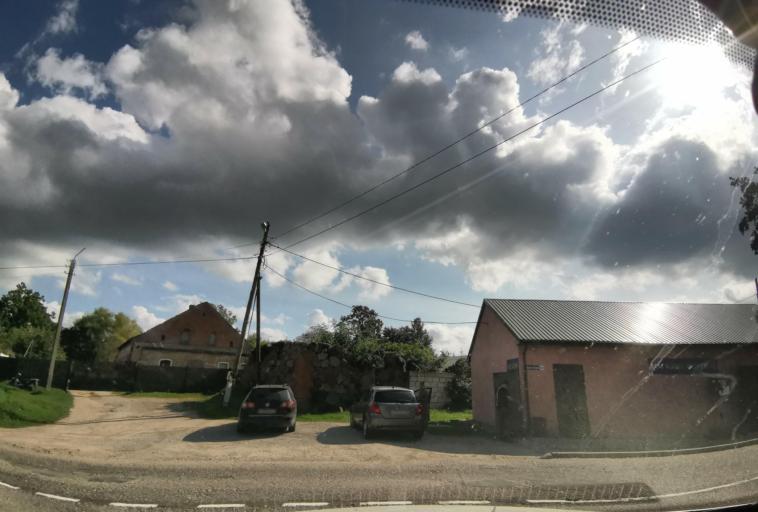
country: PL
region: Warmian-Masurian Voivodeship
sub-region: Powiat goldapski
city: Goldap
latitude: 54.4558
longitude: 22.4307
